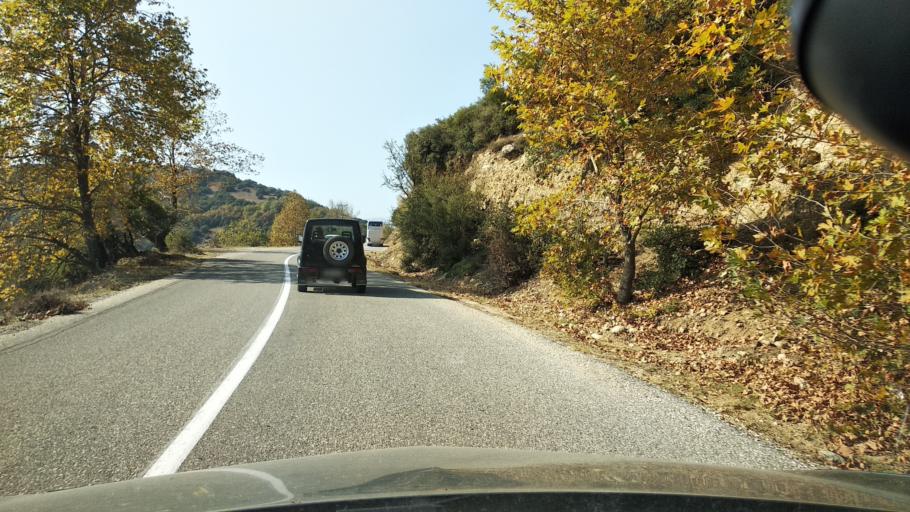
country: GR
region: Thessaly
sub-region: Trikala
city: Kalampaka
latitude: 39.7181
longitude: 21.6444
